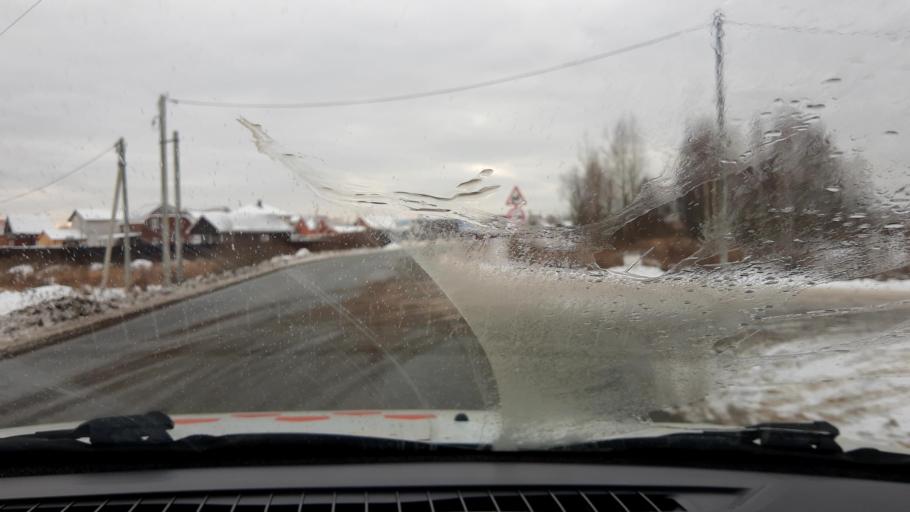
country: RU
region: Nizjnij Novgorod
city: Neklyudovo
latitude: 56.4270
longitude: 43.9634
